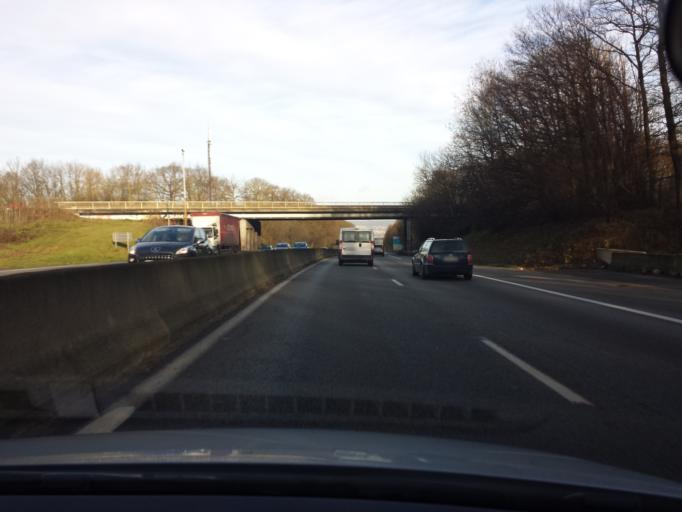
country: FR
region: Ile-de-France
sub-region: Departement des Yvelines
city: Orgeval
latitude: 48.9009
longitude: 2.0052
